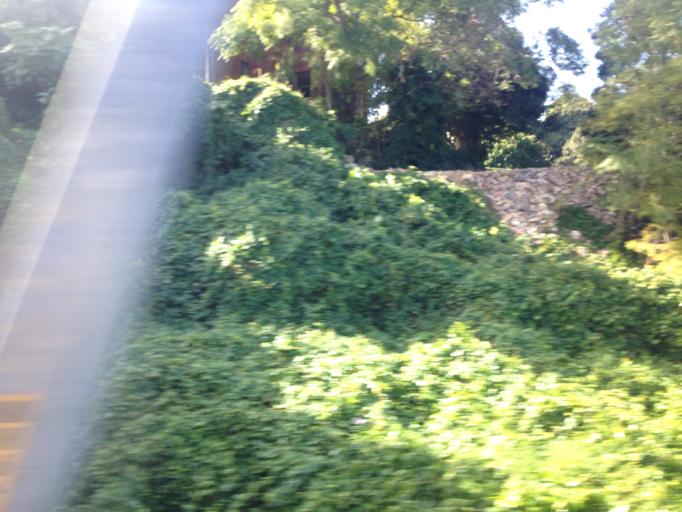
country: AU
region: New South Wales
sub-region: North Sydney
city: Wollstonecraft
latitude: -33.8346
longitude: 151.1971
